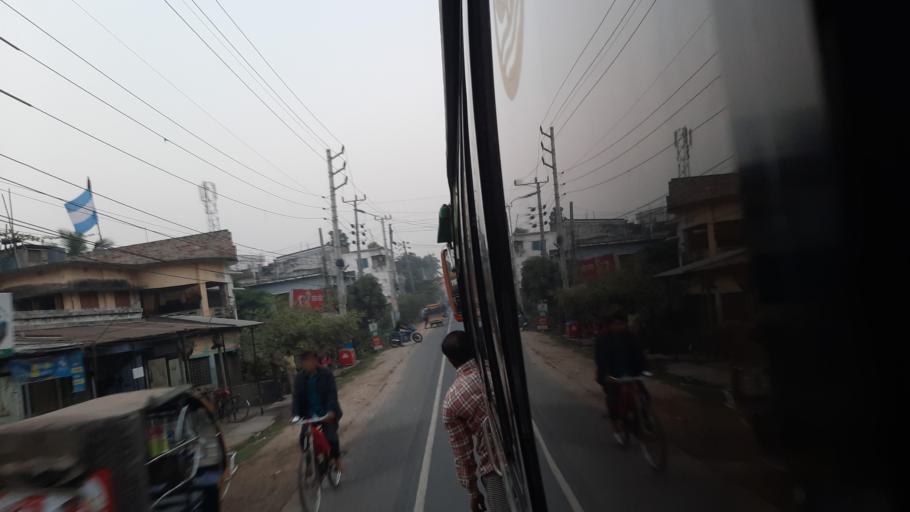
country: BD
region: Khulna
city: Jessore
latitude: 23.1772
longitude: 89.1917
